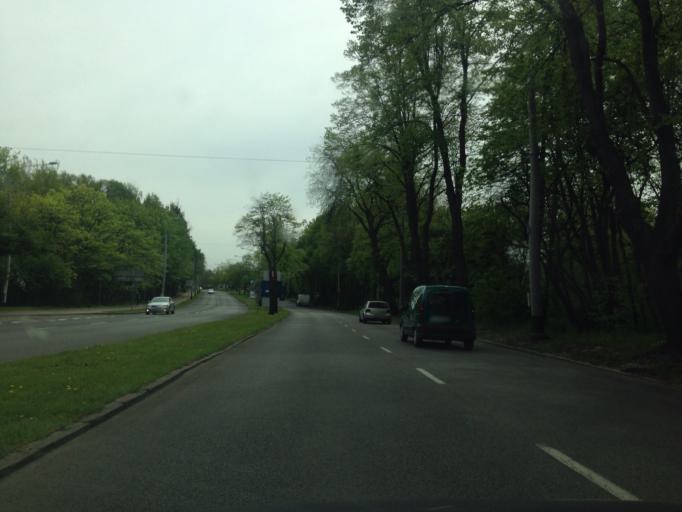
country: PL
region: Pomeranian Voivodeship
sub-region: Sopot
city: Sopot
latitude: 54.4633
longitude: 18.5539
